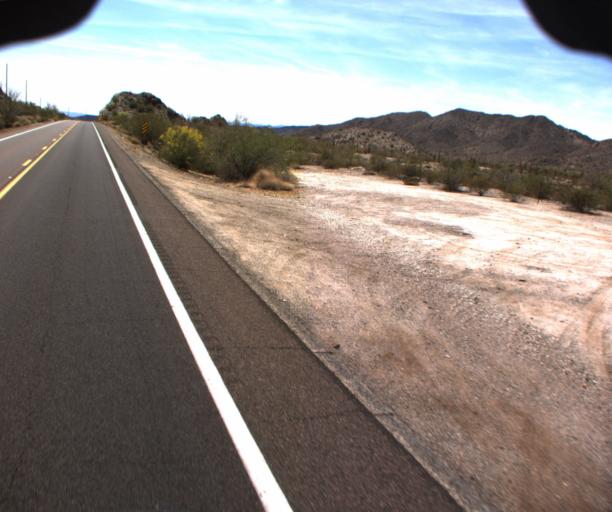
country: US
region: Arizona
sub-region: La Paz County
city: Salome
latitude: 33.7450
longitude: -113.6736
